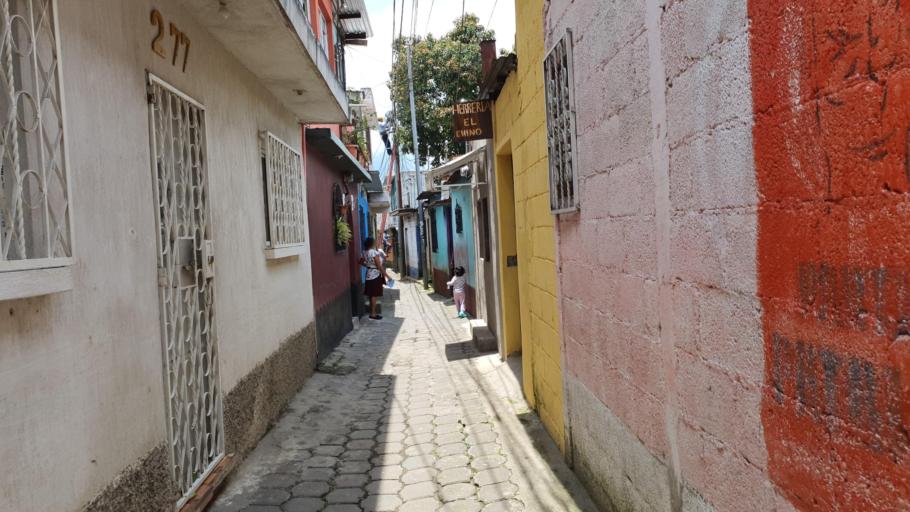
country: GT
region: Guatemala
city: Villa Canales
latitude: 14.4855
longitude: -90.5353
